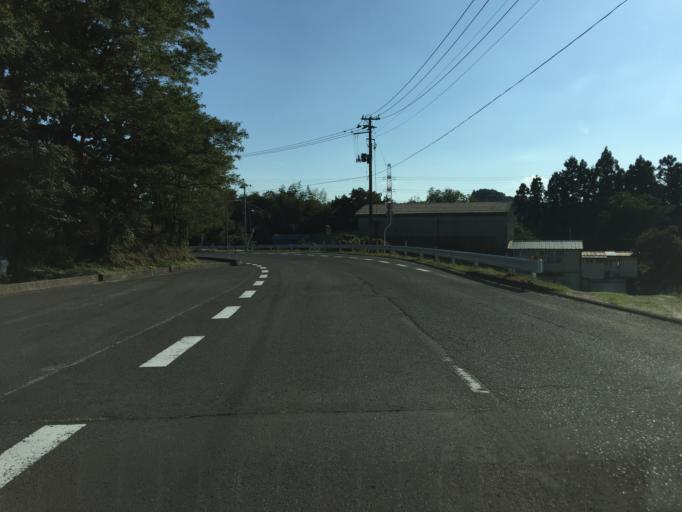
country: JP
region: Fukushima
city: Nihommatsu
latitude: 37.6490
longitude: 140.4915
